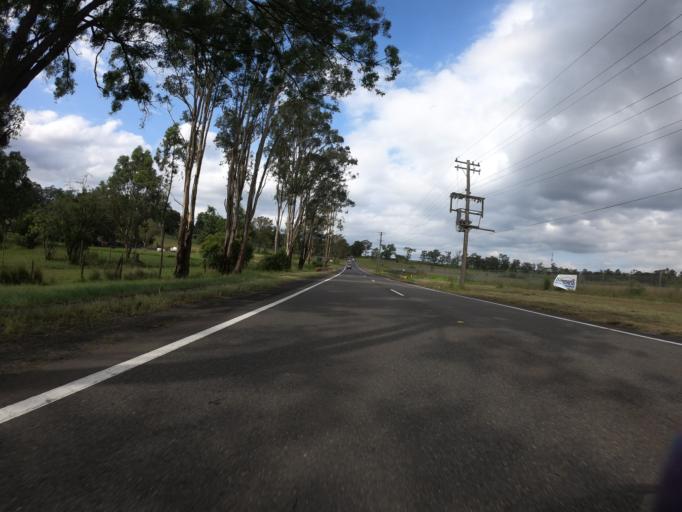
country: AU
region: New South Wales
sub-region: Blacktown
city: Riverstone
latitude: -33.6674
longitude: 150.8842
